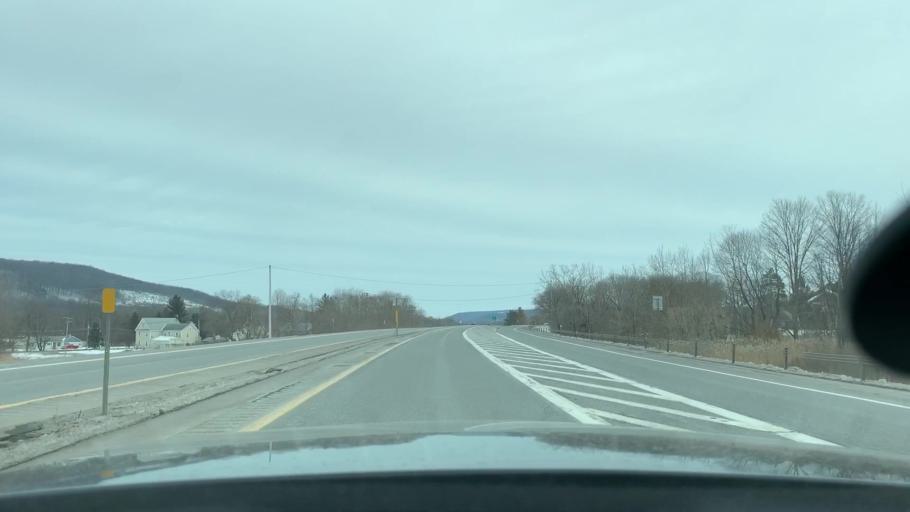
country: US
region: New York
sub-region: Herkimer County
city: Frankfort
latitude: 43.0244
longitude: -75.0589
